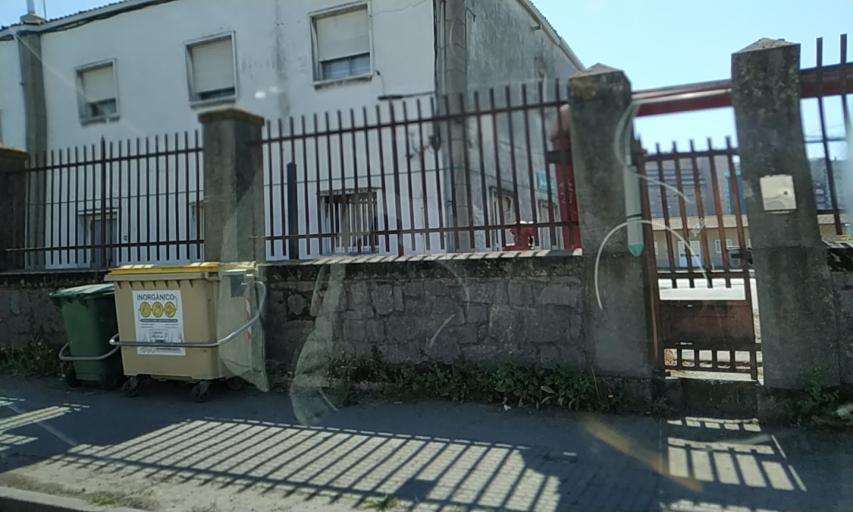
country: ES
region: Galicia
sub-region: Provincia da Coruna
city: A Coruna
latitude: 43.3571
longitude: -8.3946
